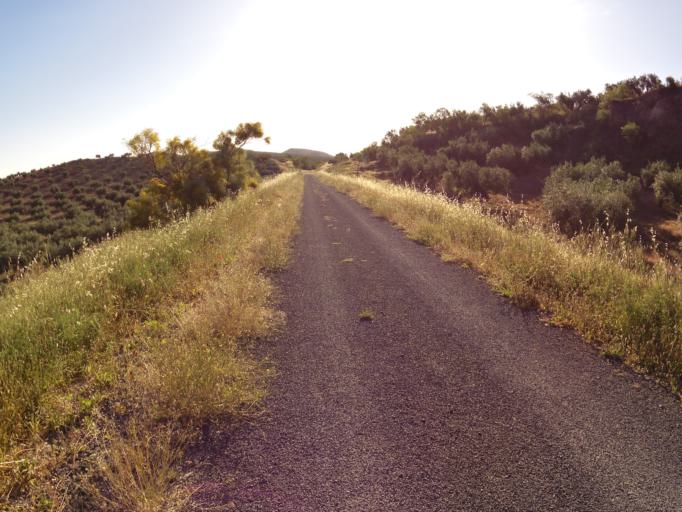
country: ES
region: Andalusia
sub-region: Province of Cordoba
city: Luque
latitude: 37.5722
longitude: -4.2726
